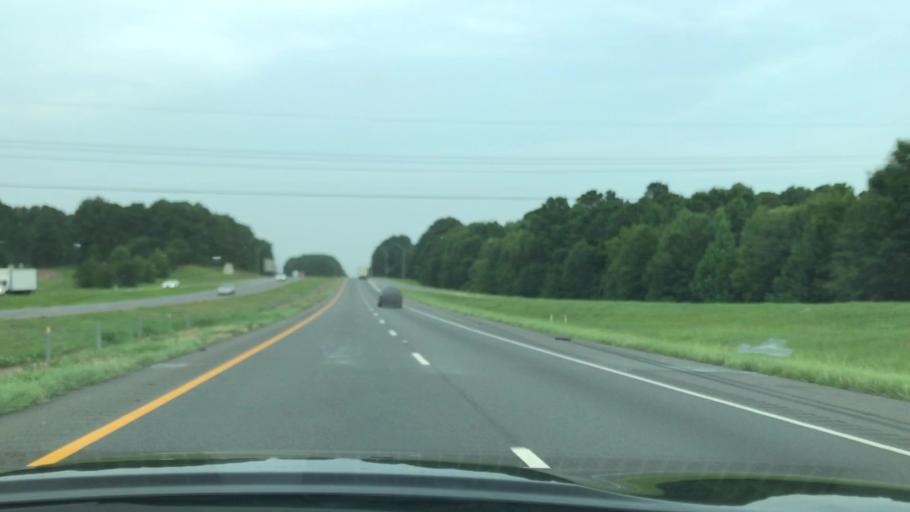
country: US
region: Texas
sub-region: Harrison County
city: Marshall
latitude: 32.4911
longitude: -94.3606
